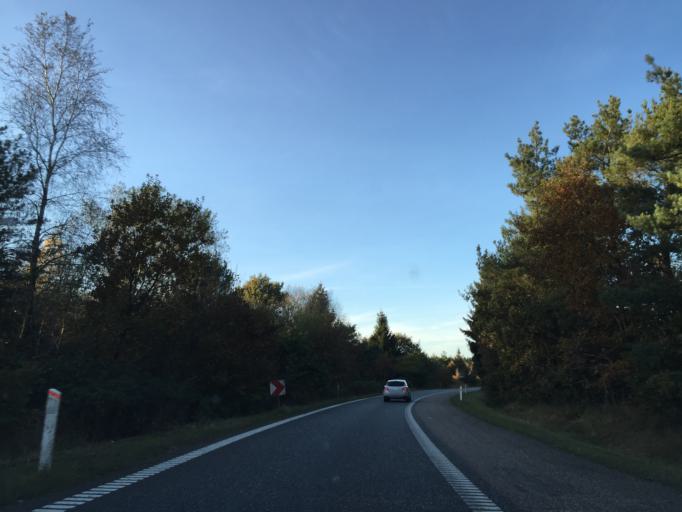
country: DK
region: South Denmark
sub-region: Aabenraa Kommune
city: Krusa
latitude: 54.8750
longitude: 9.3796
